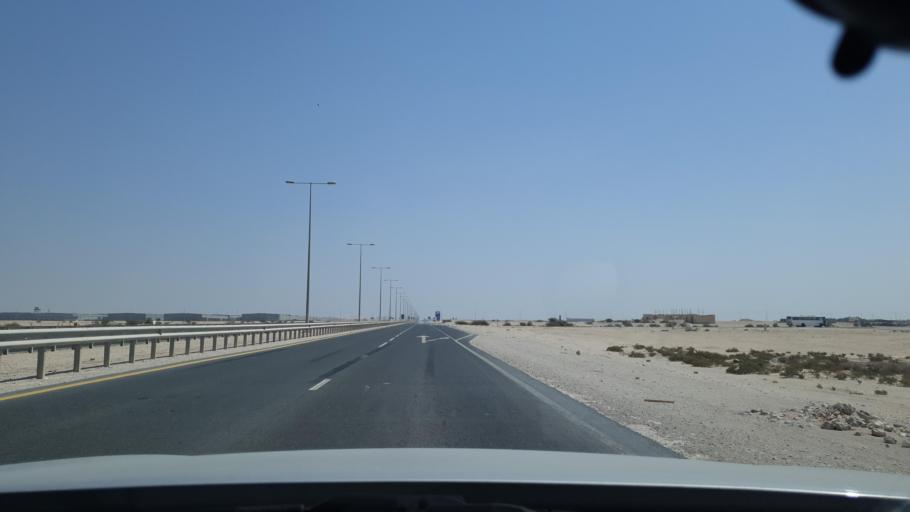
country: QA
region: Baladiyat Umm Salal
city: Umm Salal Muhammad
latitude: 25.3882
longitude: 51.3419
